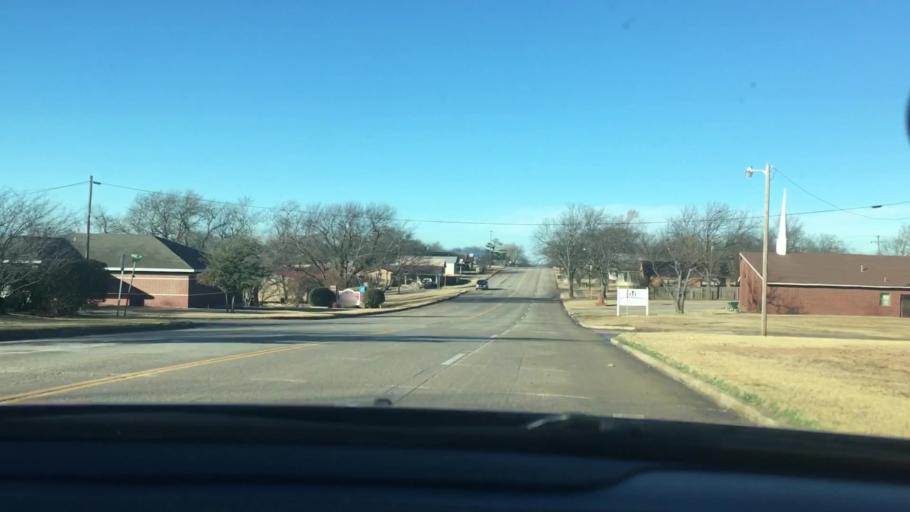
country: US
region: Oklahoma
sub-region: Murray County
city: Sulphur
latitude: 34.5110
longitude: -96.9583
